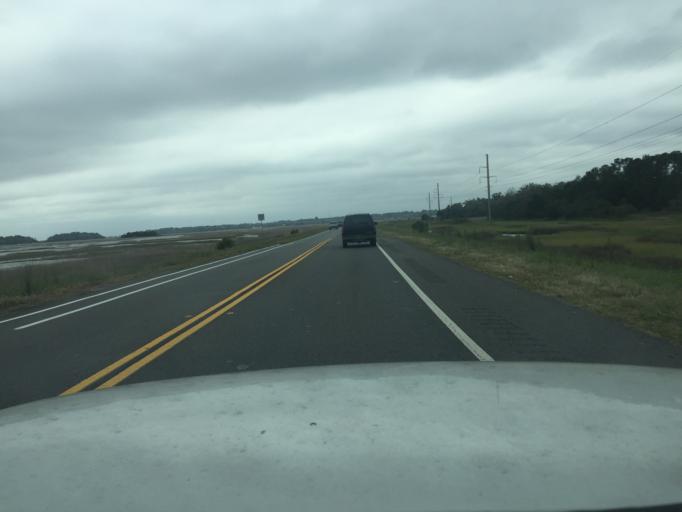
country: US
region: Georgia
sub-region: Chatham County
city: Skidaway Island
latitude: 31.9501
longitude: -81.0718
